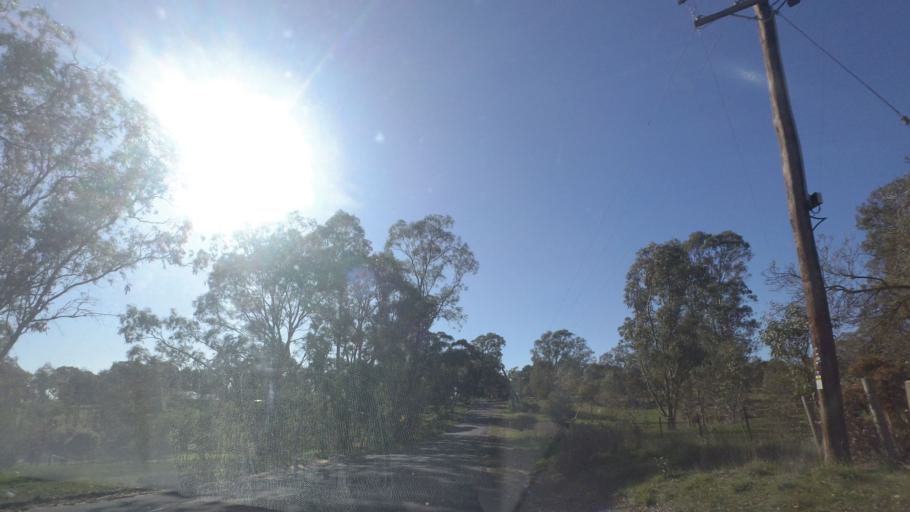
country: AU
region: Victoria
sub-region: Mount Alexander
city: Castlemaine
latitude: -37.1070
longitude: 144.4201
